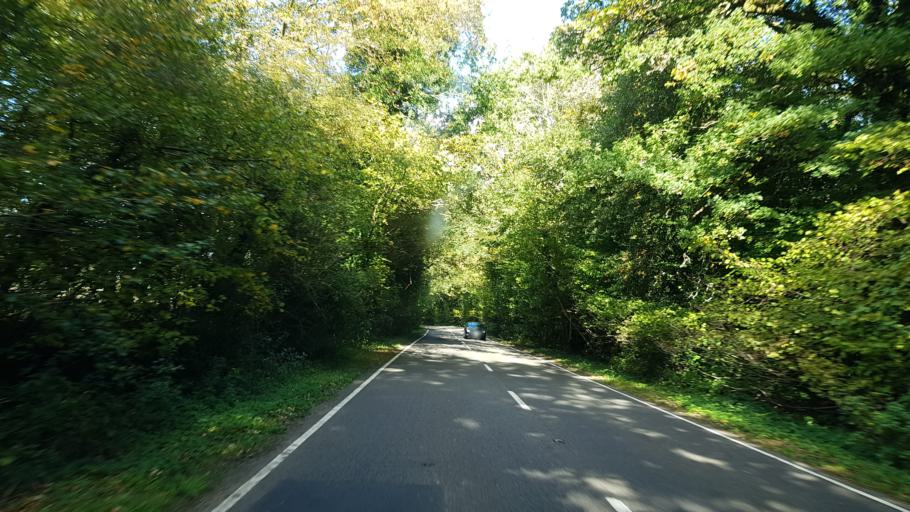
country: GB
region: England
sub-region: Surrey
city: Chiddingfold
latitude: 51.0926
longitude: -0.6423
